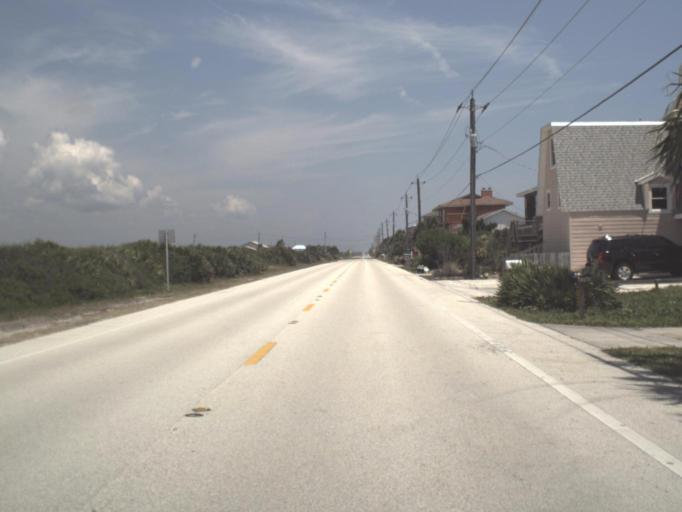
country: US
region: Florida
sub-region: Saint Johns County
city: Villano Beach
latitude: 30.0167
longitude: -81.3218
